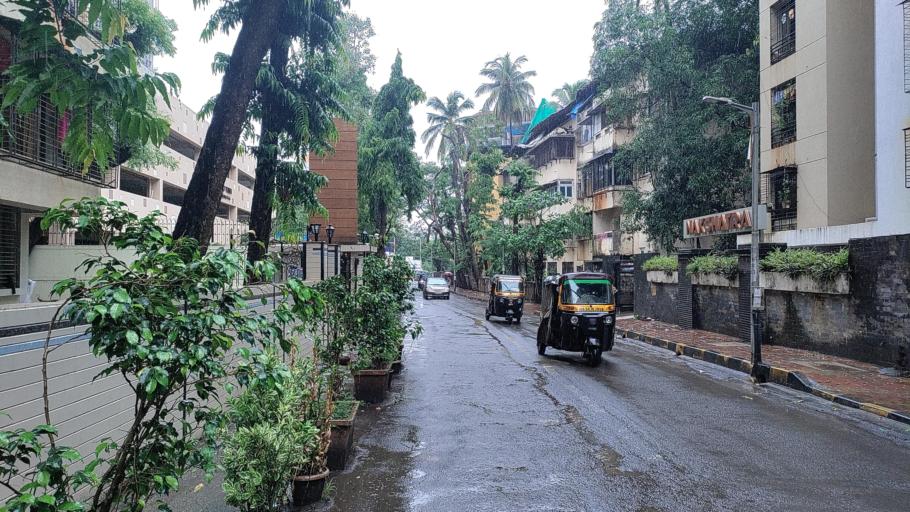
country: IN
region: Maharashtra
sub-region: Mumbai Suburban
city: Borivli
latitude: 19.2366
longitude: 72.8564
